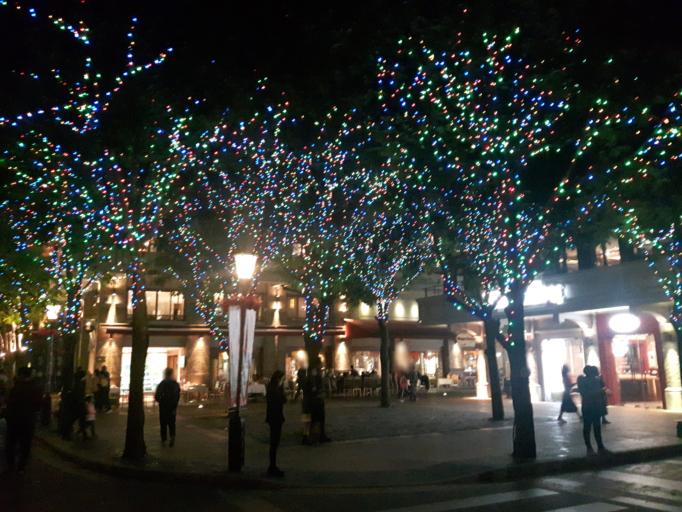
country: CN
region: Guangdong
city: Zumiao
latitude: 23.0326
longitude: 113.1095
